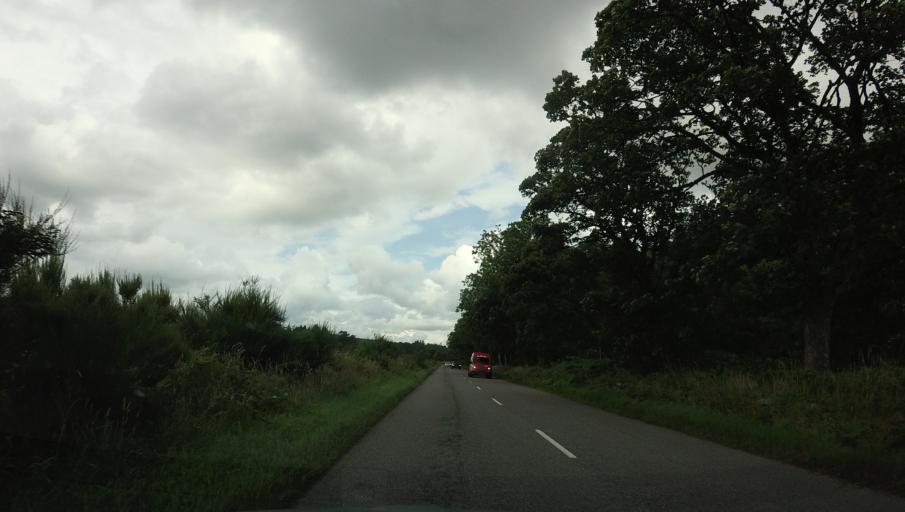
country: GB
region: Scotland
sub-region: Aberdeenshire
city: Torphins
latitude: 57.0612
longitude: -2.6409
